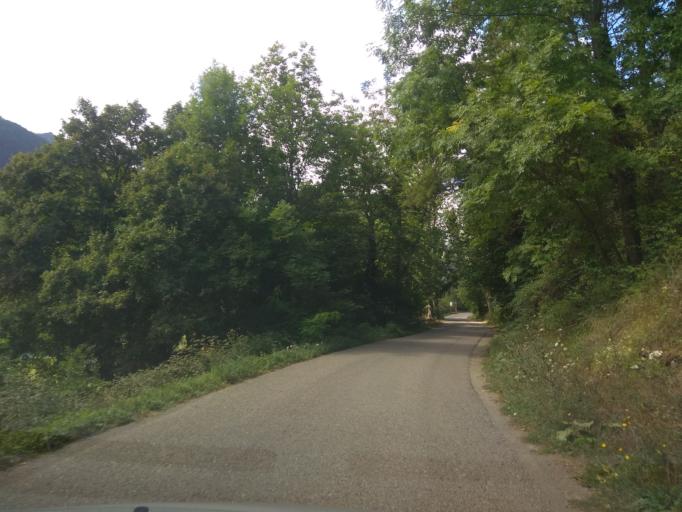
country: ES
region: Catalonia
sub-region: Provincia de Lleida
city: Les
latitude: 42.7337
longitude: 0.7210
